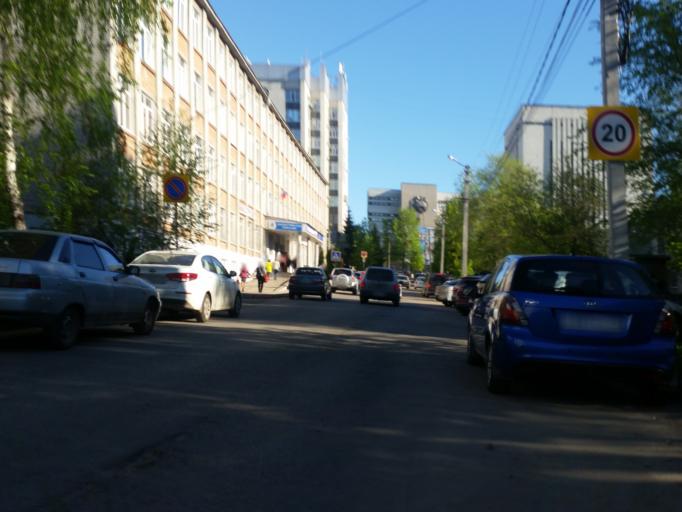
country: RU
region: Ulyanovsk
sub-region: Ulyanovskiy Rayon
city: Ulyanovsk
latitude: 54.3106
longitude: 48.3937
